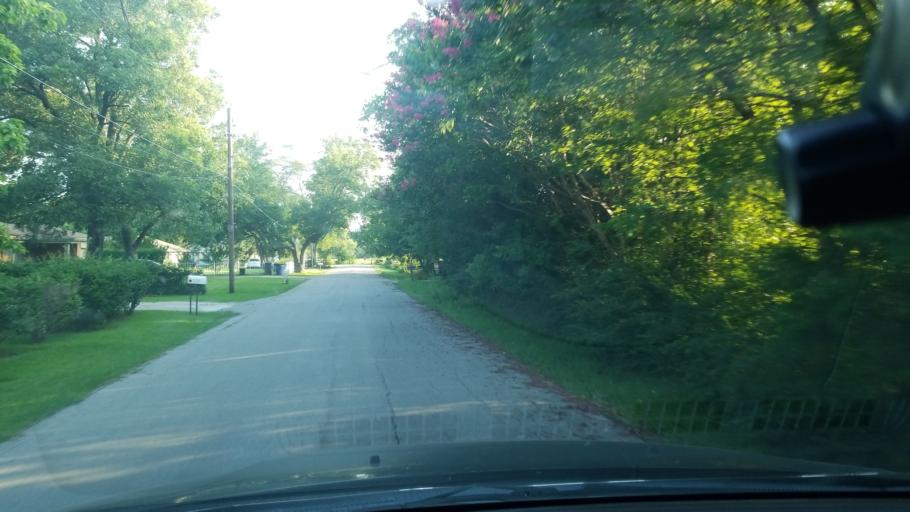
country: US
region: Texas
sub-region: Dallas County
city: Balch Springs
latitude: 32.7235
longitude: -96.6649
